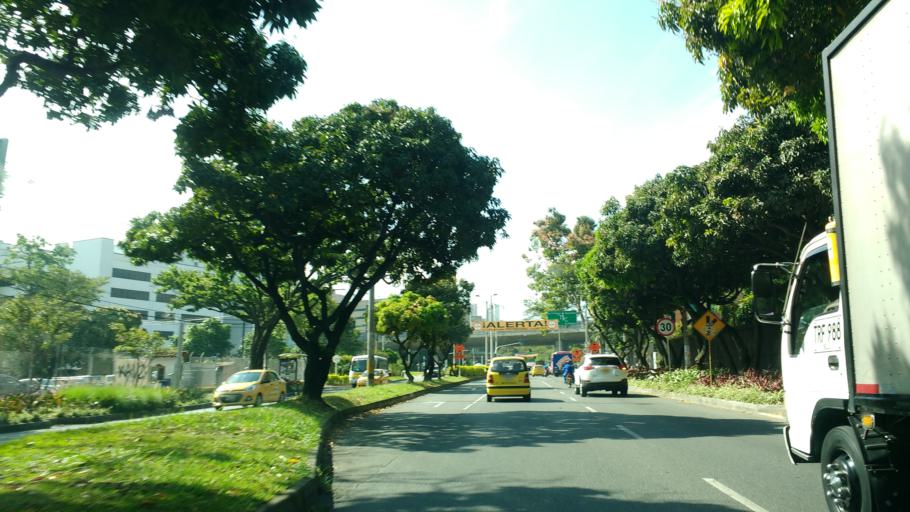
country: CO
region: Antioquia
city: Itagui
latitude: 6.2046
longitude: -75.5771
